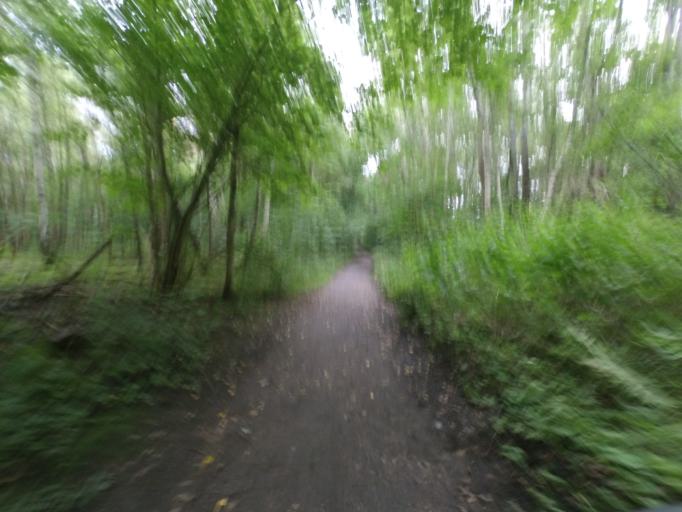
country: DE
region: Schleswig-Holstein
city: Glinde
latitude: 53.5009
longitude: 10.1844
